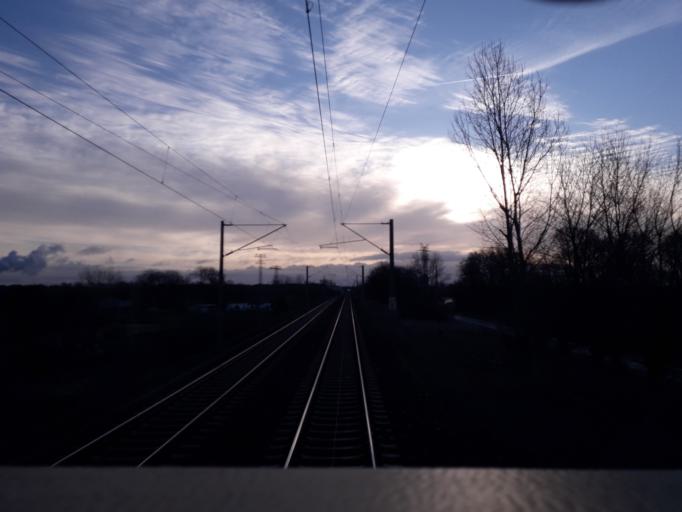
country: DE
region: Brandenburg
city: Brieselang
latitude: 52.5933
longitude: 12.9601
